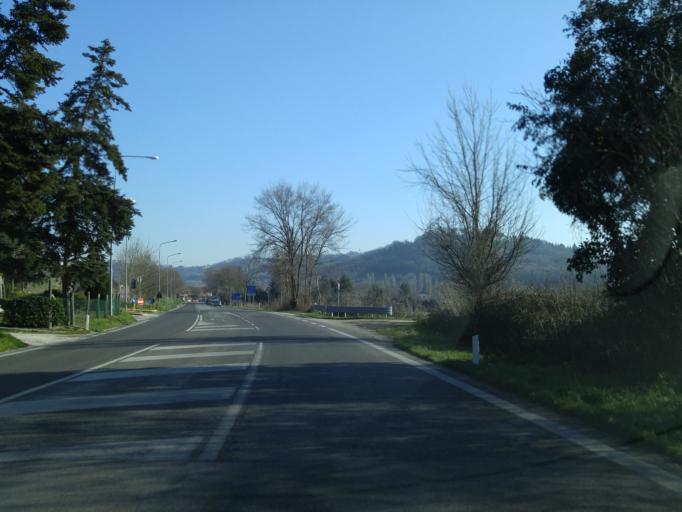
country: IT
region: The Marches
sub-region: Provincia di Pesaro e Urbino
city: Gradara
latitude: 43.9505
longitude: 12.7865
